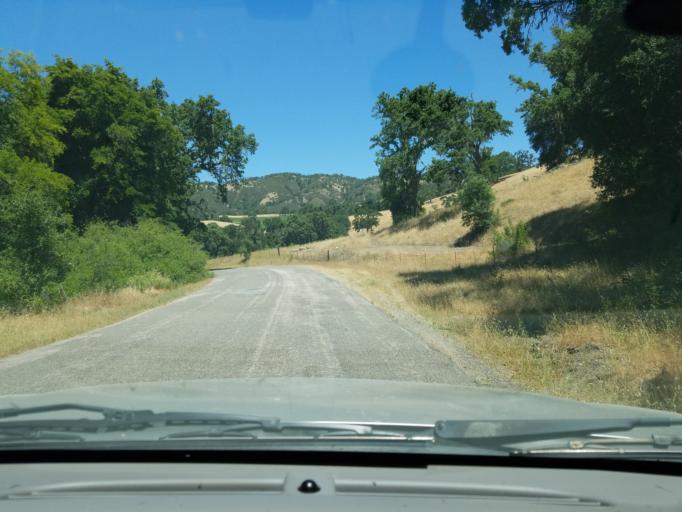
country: US
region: California
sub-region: Monterey County
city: Gonzales
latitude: 36.3497
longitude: -121.5427
